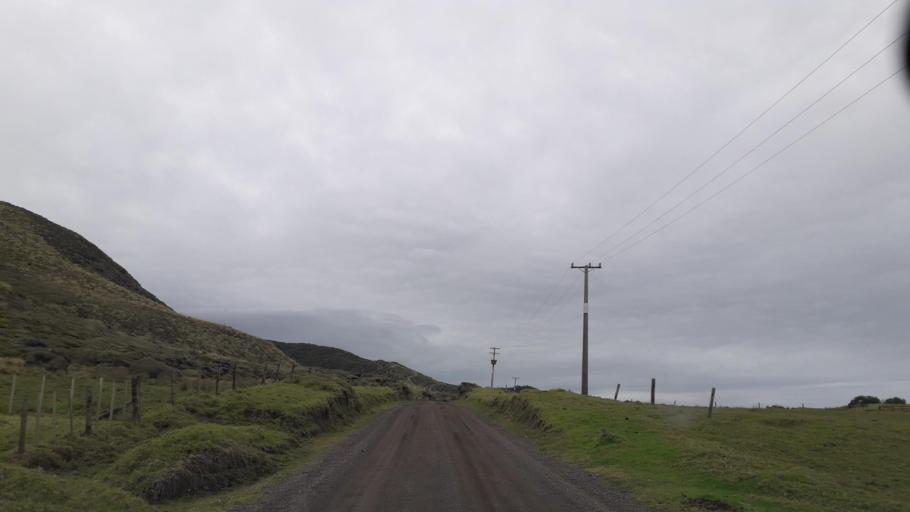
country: NZ
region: Northland
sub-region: Far North District
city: Ahipara
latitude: -35.4303
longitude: 173.2763
